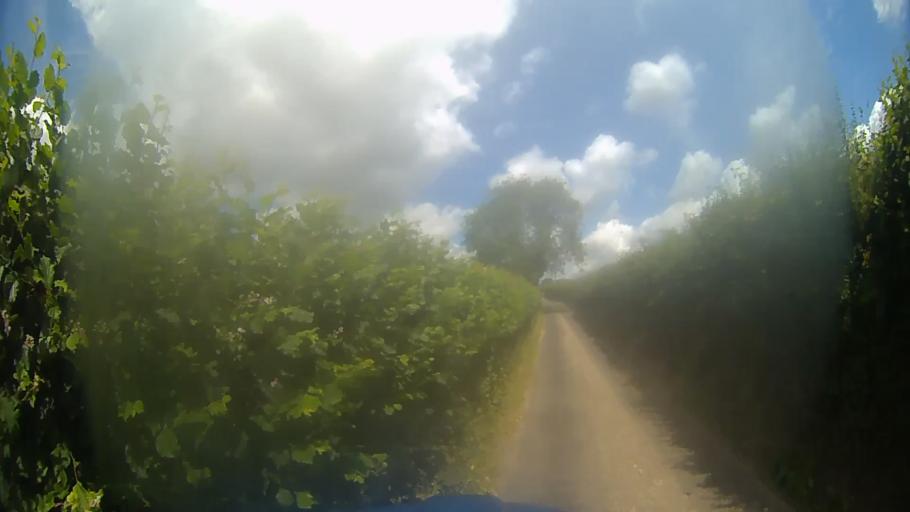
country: GB
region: England
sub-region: Hampshire
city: Andover
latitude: 51.2493
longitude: -1.4396
